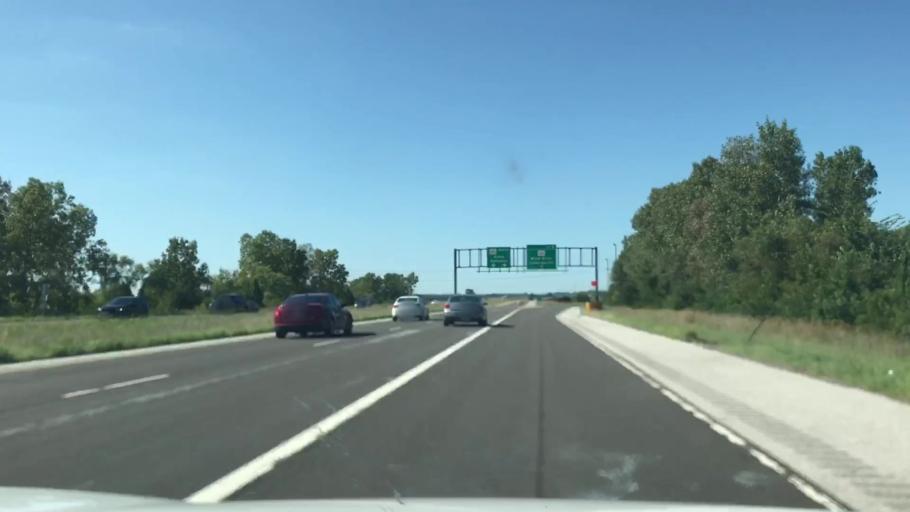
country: US
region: Illinois
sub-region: Madison County
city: South Roxana
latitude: 38.8456
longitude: -90.0477
